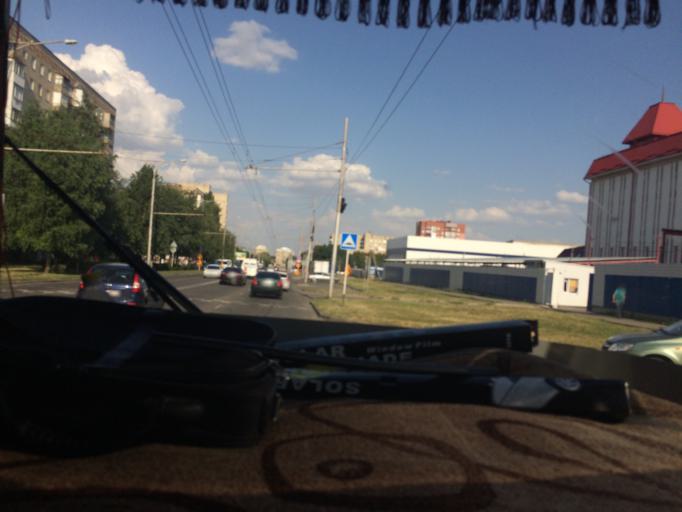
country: RU
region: Stavropol'skiy
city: Stavropol'
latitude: 45.0136
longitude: 41.9196
